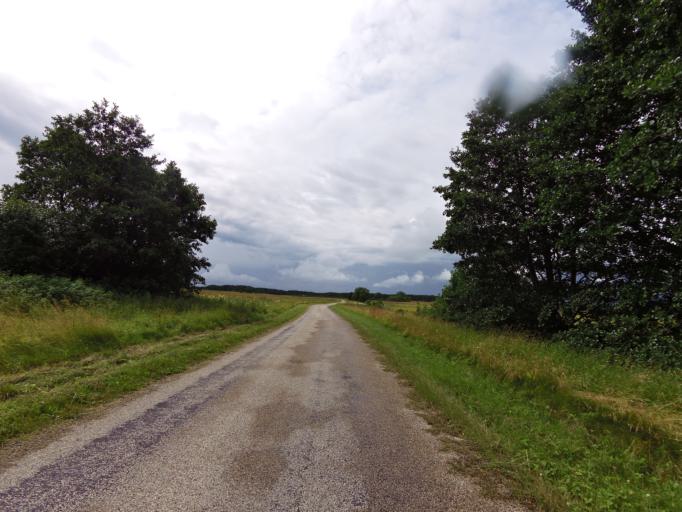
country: EE
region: Laeaene
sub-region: Vormsi vald
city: Hullo
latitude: 58.9858
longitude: 23.3141
